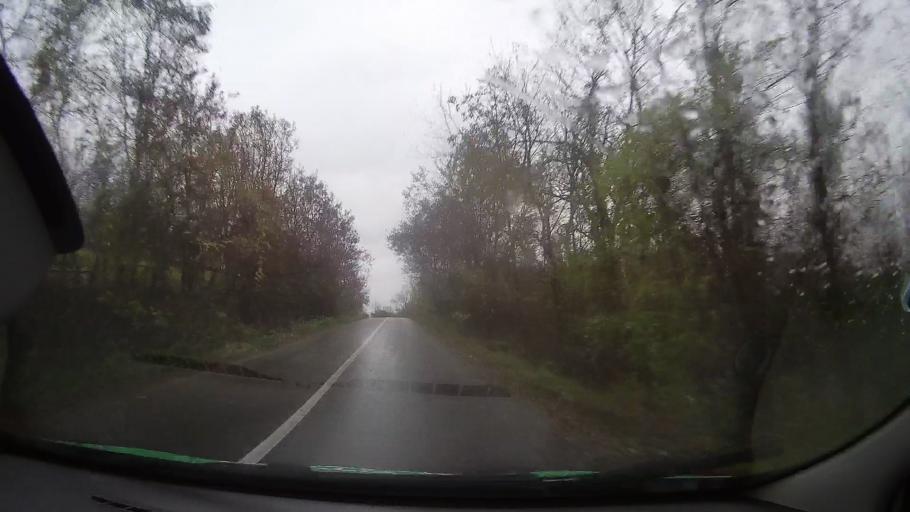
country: RO
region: Mures
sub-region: Comuna Brancovenesti
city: Valenii de Mures
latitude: 46.8976
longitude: 24.7952
